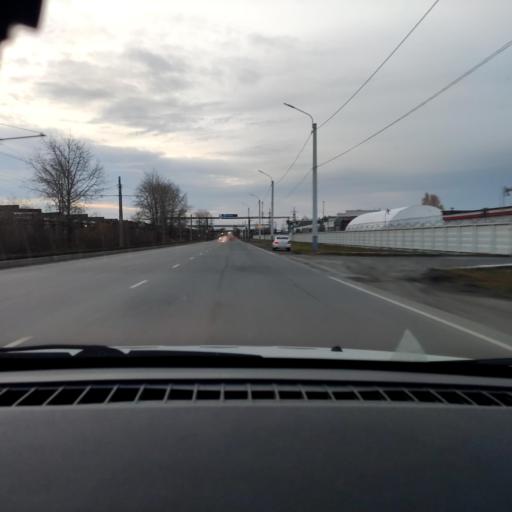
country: RU
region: Perm
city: Gamovo
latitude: 57.9168
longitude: 56.1509
